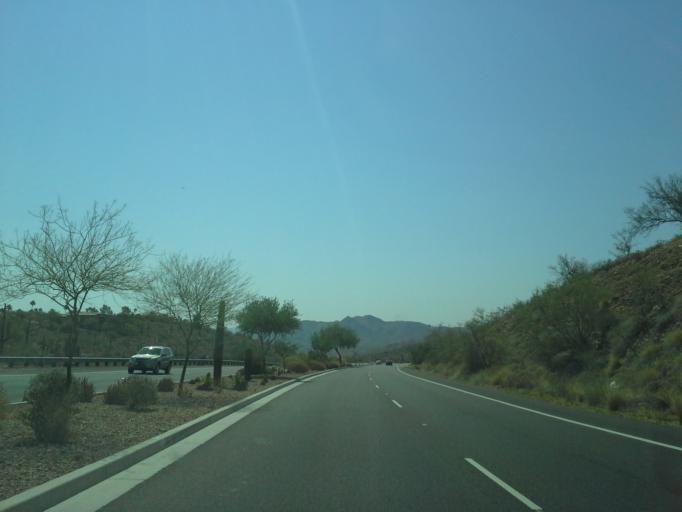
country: US
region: Arizona
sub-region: Maricopa County
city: Fountain Hills
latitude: 33.5806
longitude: -111.7310
